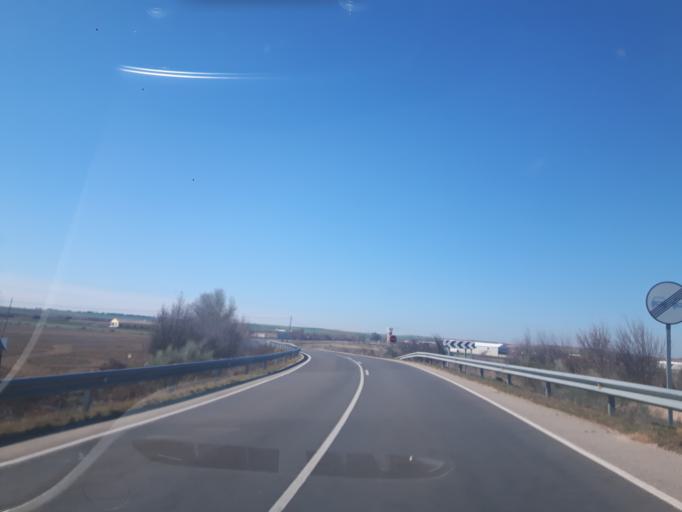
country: ES
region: Castille and Leon
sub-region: Provincia de Salamanca
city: Garcihernandez
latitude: 40.8622
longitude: -5.4198
